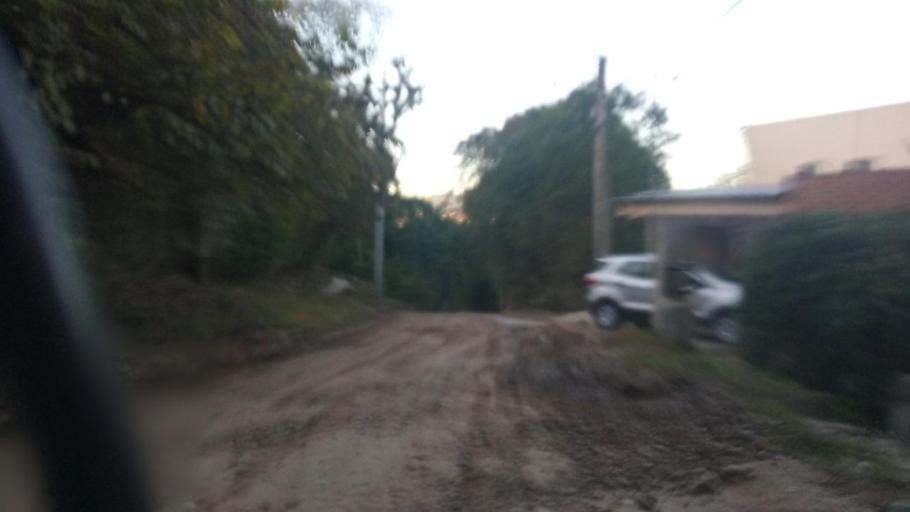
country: AR
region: Jujuy
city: San Salvador de Jujuy
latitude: -24.1663
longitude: -65.3150
